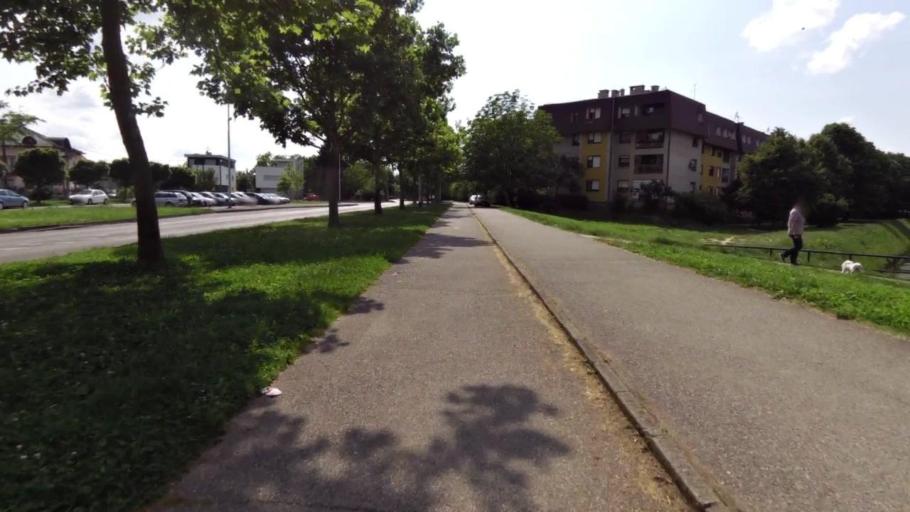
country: HR
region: Grad Zagreb
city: Jankomir
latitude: 45.7839
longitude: 15.9342
